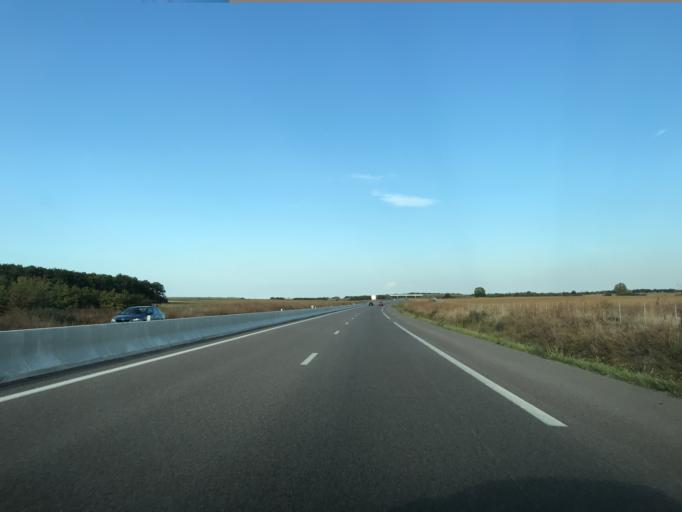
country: FR
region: Lorraine
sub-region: Departement de Meurthe-et-Moselle
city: Conflans-en-Jarnisy
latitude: 49.1708
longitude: 5.7565
